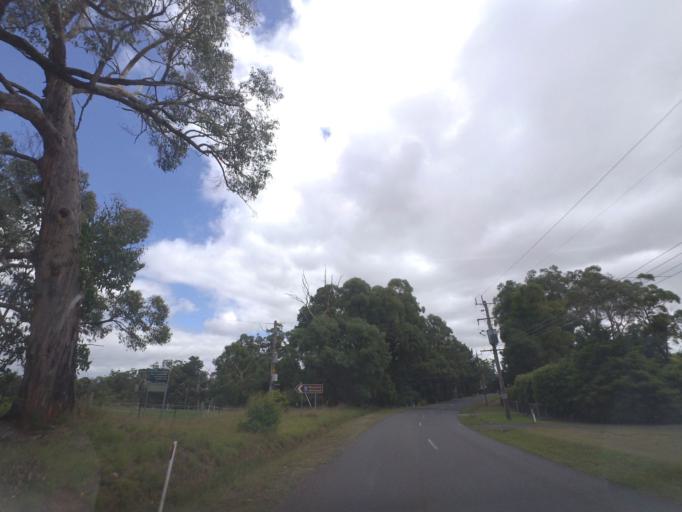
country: AU
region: Victoria
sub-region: Yarra Ranges
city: Launching Place
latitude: -37.8035
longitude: 145.5551
